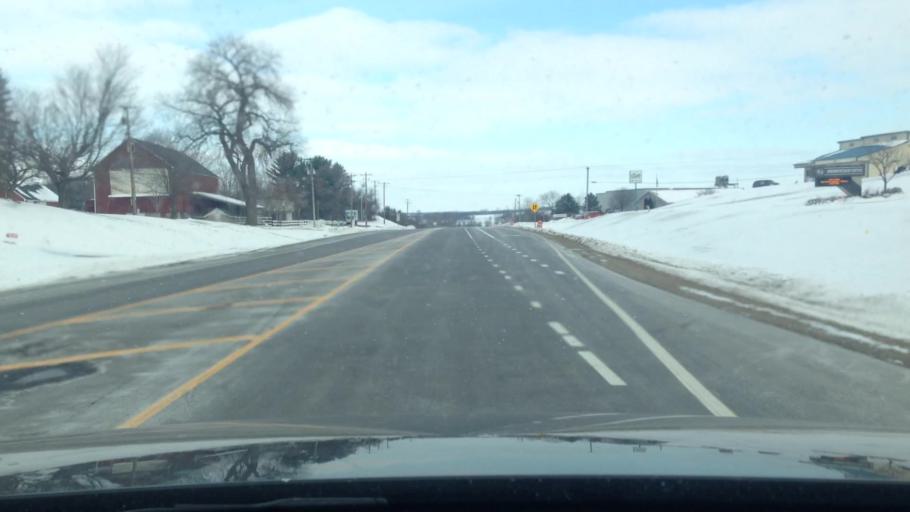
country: US
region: Wisconsin
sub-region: Walworth County
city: Lake Geneva
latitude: 42.6142
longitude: -88.4157
